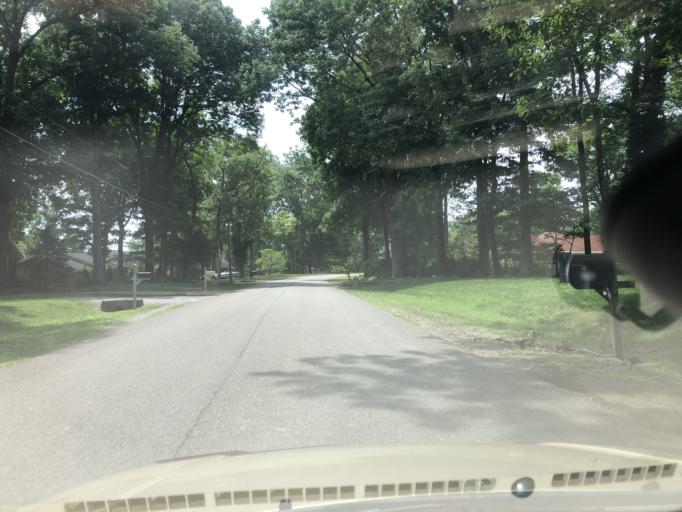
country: US
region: Tennessee
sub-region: Davidson County
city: Lakewood
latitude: 36.2555
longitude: -86.5883
